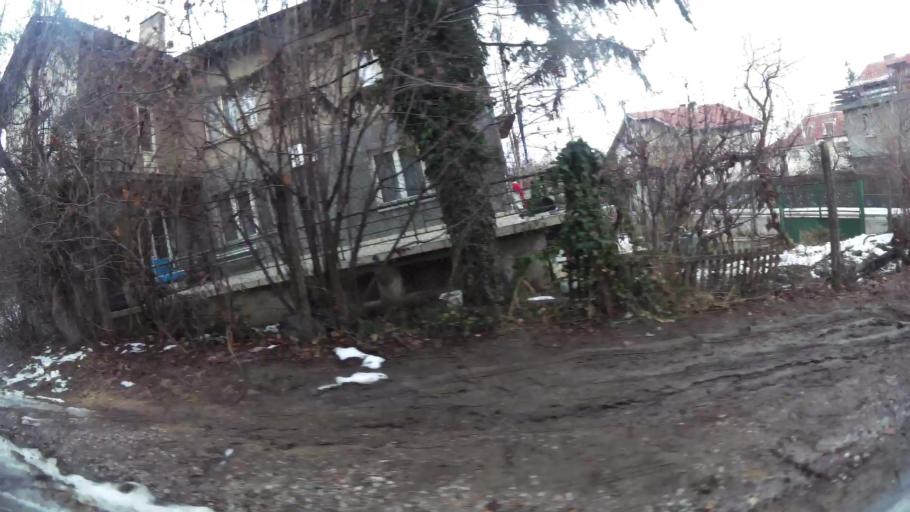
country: BG
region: Sofia-Capital
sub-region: Stolichna Obshtina
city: Sofia
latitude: 42.6645
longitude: 23.2425
